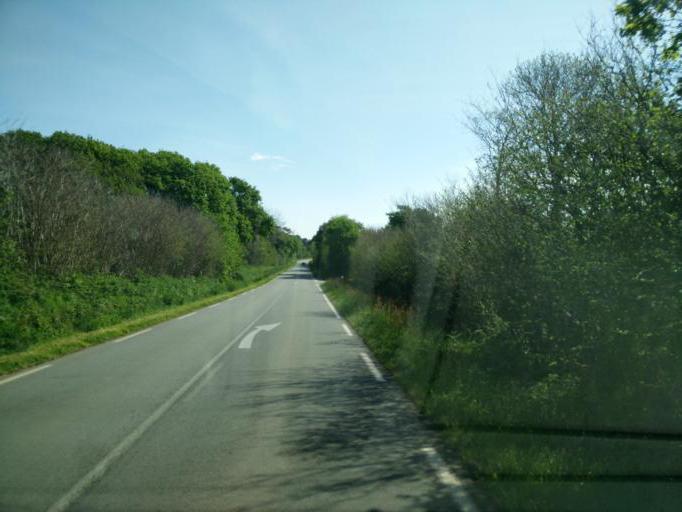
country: FR
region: Brittany
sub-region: Departement du Finistere
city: Plomodiern
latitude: 48.2230
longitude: -4.2827
